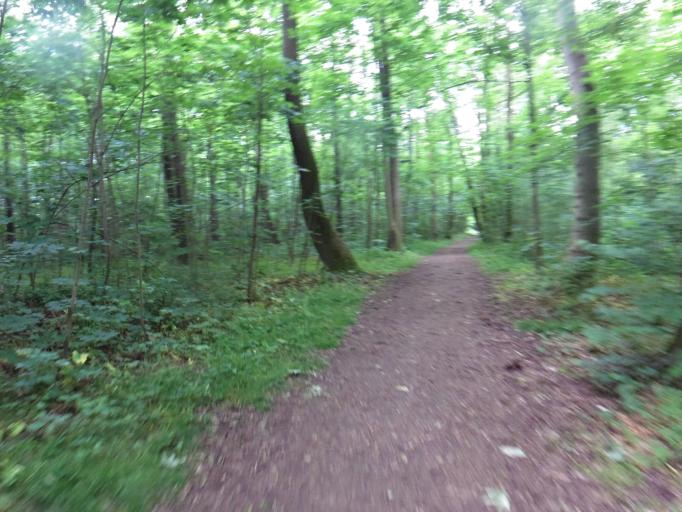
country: DE
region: Saxony
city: Markkleeberg
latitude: 51.3086
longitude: 12.3372
